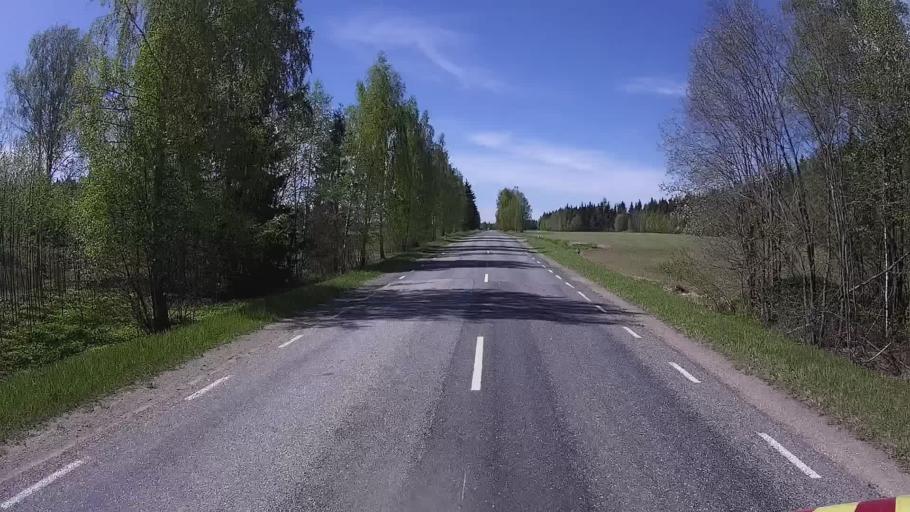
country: EE
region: Polvamaa
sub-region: Raepina vald
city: Rapina
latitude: 57.9815
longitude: 27.3078
